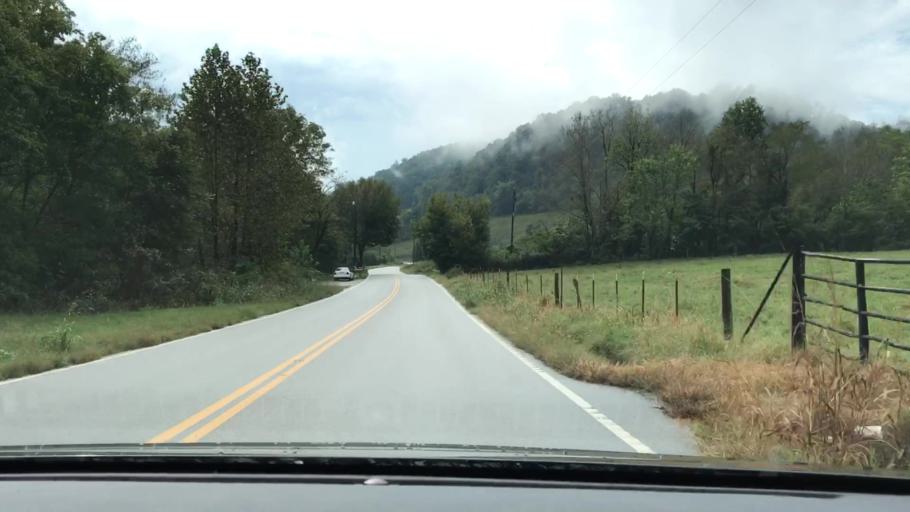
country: US
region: Tennessee
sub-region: Macon County
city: Lafayette
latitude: 36.4007
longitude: -85.9441
